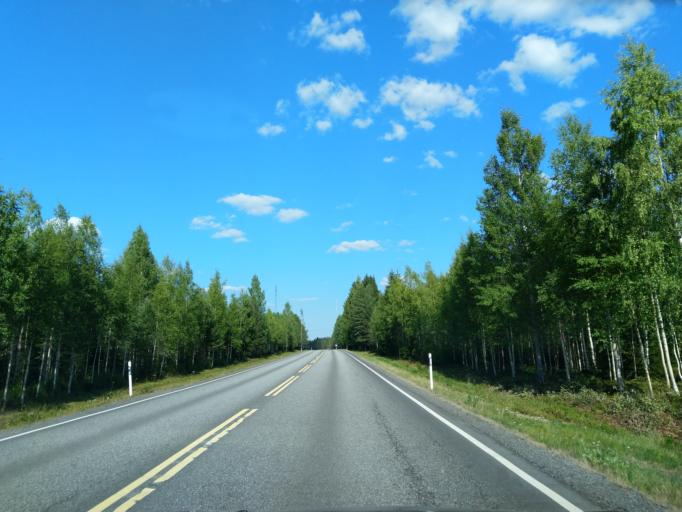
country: FI
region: Pirkanmaa
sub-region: Luoteis-Pirkanmaa
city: Kihnioe
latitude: 62.1998
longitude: 23.2012
